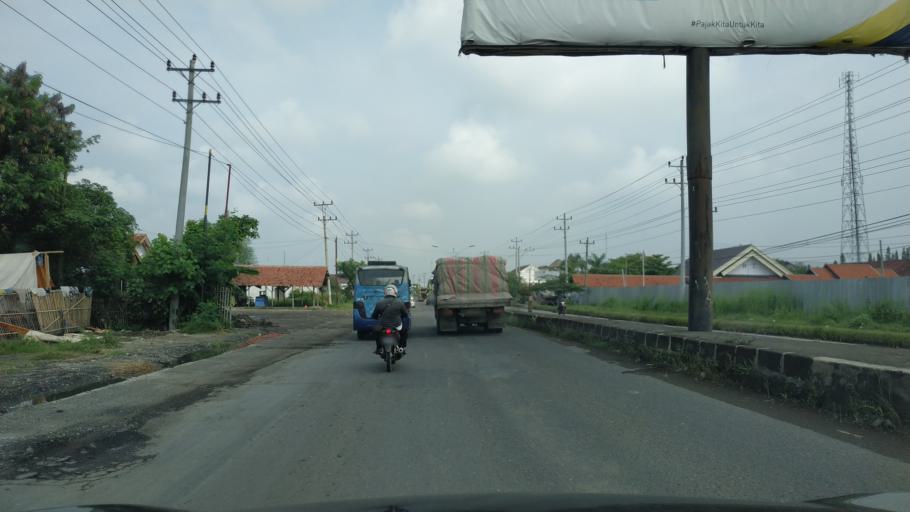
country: ID
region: Central Java
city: Bulakamba
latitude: -6.8715
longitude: 108.8987
